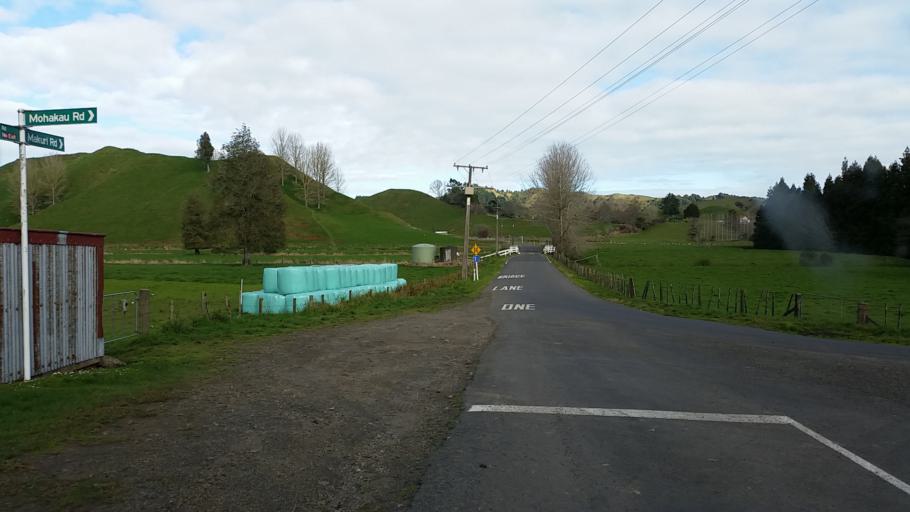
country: NZ
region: Taranaki
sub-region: South Taranaki District
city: Eltham
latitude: -39.2525
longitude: 174.5077
